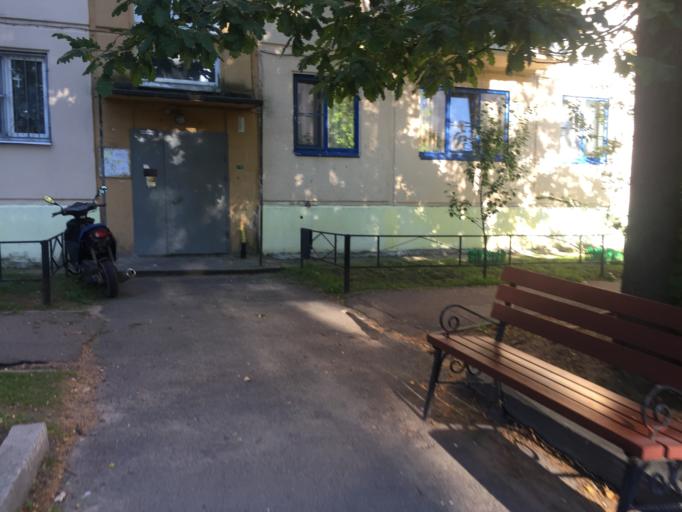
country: RU
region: Leningrad
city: Murino
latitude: 60.0388
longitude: 30.4651
